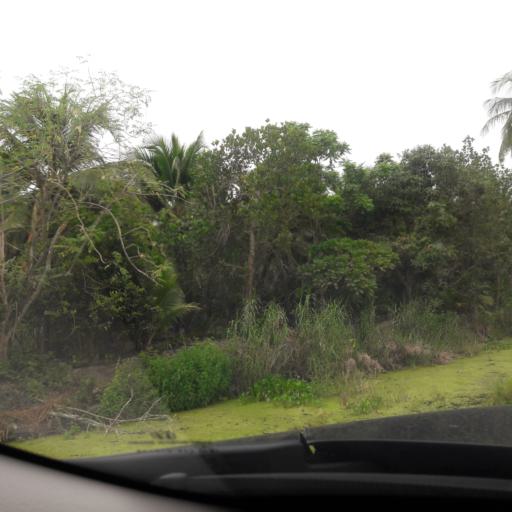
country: TH
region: Ratchaburi
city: Damnoen Saduak
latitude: 13.5761
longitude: 99.9404
